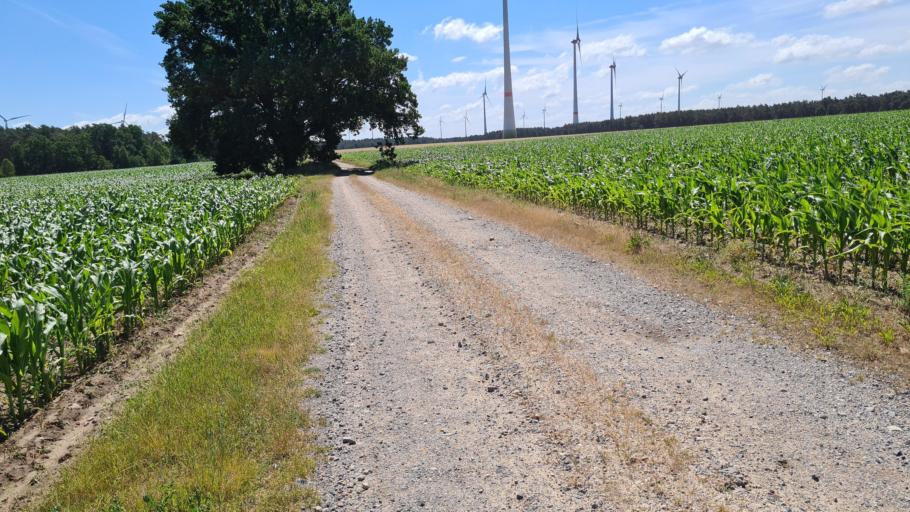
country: DE
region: Brandenburg
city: Treuenbrietzen
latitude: 52.0299
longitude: 12.8516
